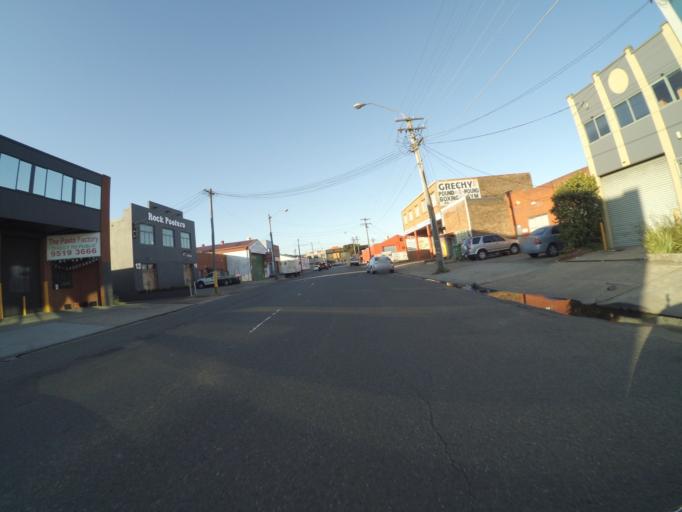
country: AU
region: New South Wales
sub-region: Marrickville
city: Marrickville
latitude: -33.9133
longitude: 151.1649
